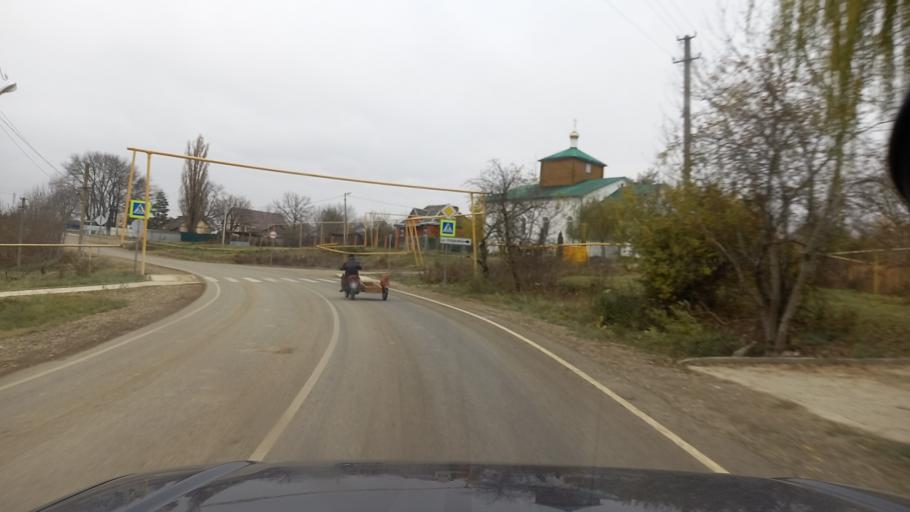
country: RU
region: Krasnodarskiy
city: Goryachiy Klyuch
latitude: 44.5193
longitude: 39.2919
